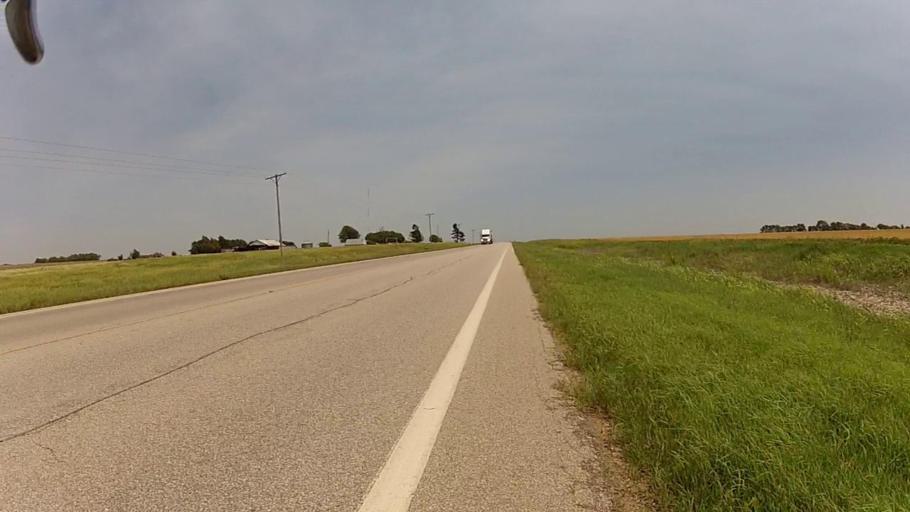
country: US
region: Kansas
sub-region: Cowley County
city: Arkansas City
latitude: 37.0565
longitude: -97.1065
